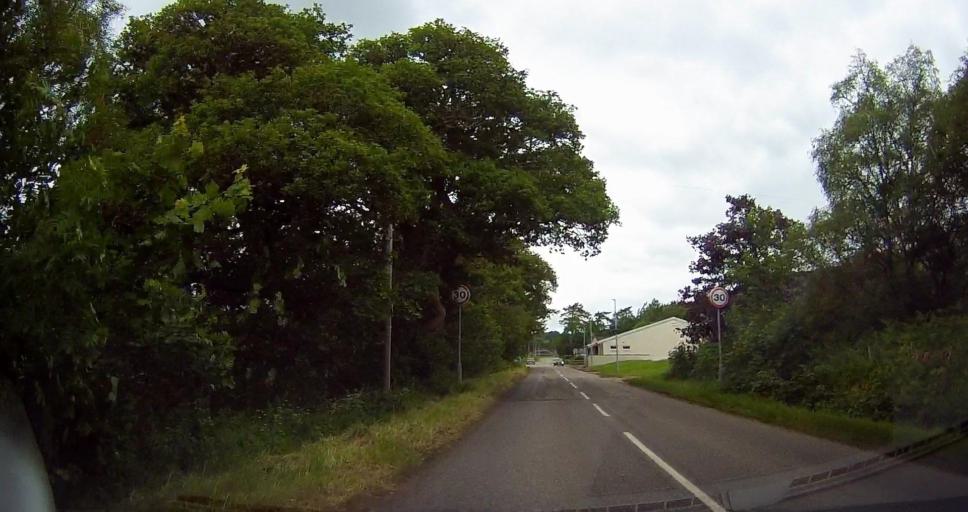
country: GB
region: Scotland
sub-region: Highland
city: Dornoch
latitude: 57.9858
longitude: -4.1516
